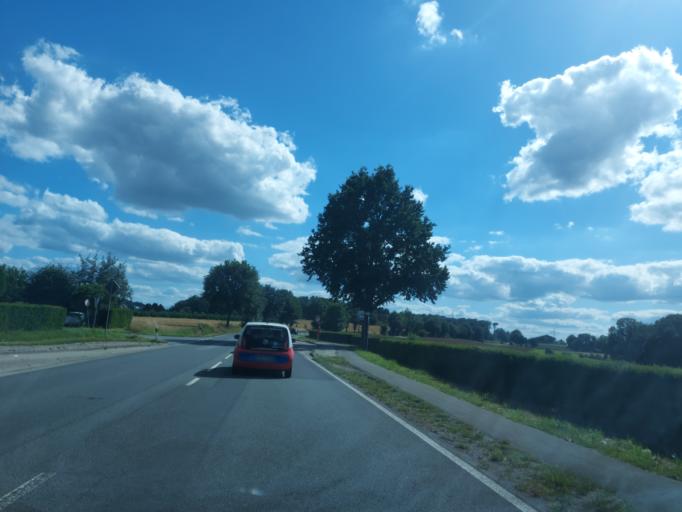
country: DE
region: Lower Saxony
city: Hagen
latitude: 52.2130
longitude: 7.9971
